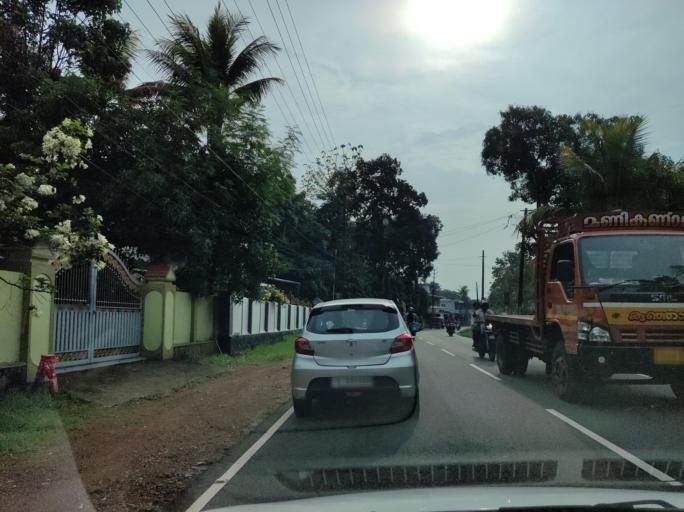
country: IN
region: Kerala
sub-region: Alappuzha
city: Kattanam
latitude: 9.1733
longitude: 76.5886
